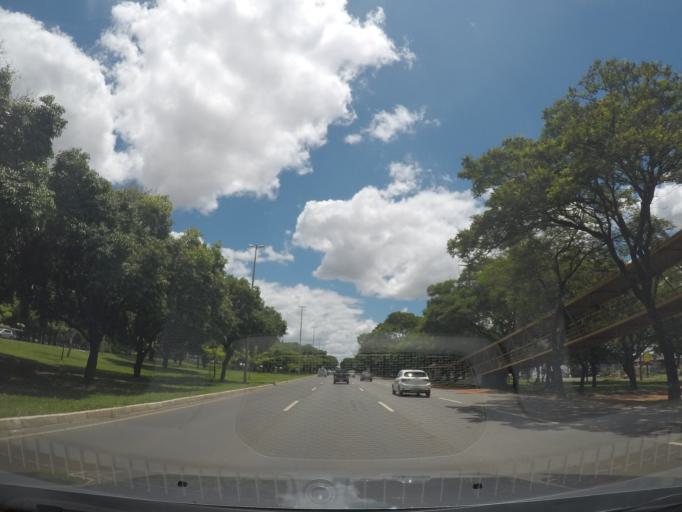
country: BR
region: Federal District
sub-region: Brasilia
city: Brasilia
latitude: -15.7959
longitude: -47.9450
